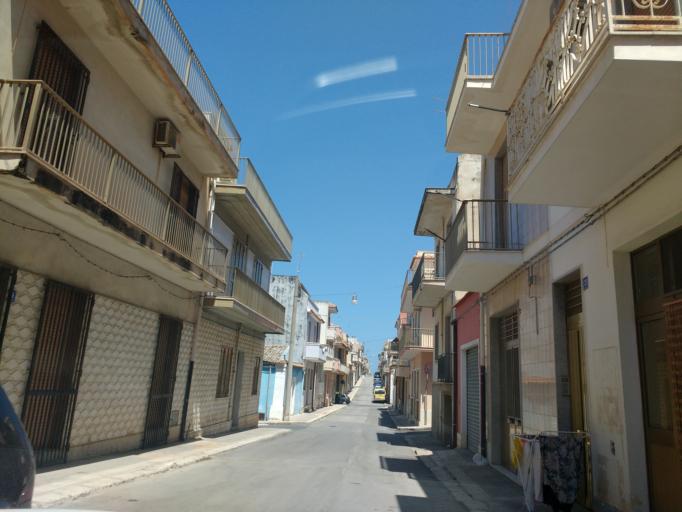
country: IT
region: Sicily
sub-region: Provincia di Siracusa
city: Pachino
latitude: 36.7168
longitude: 15.0943
